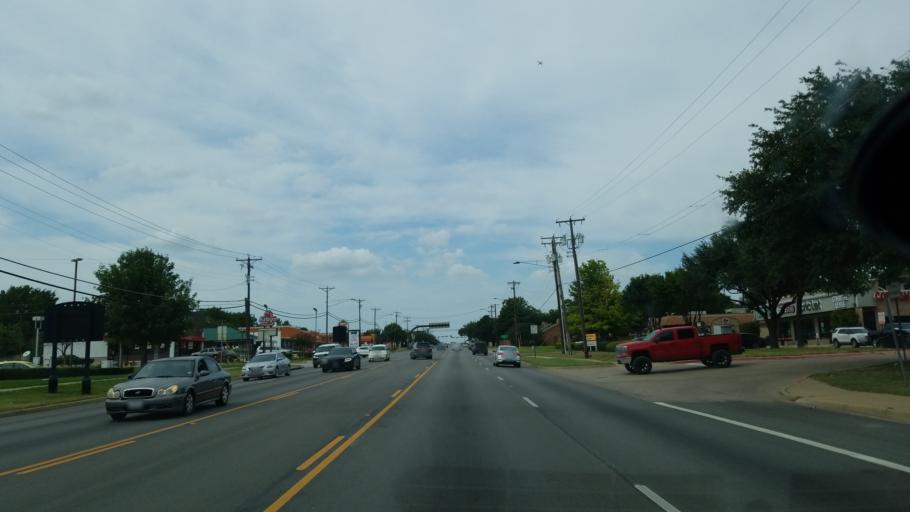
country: US
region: Texas
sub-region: Tarrant County
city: Arlington
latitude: 32.7508
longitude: -97.0973
